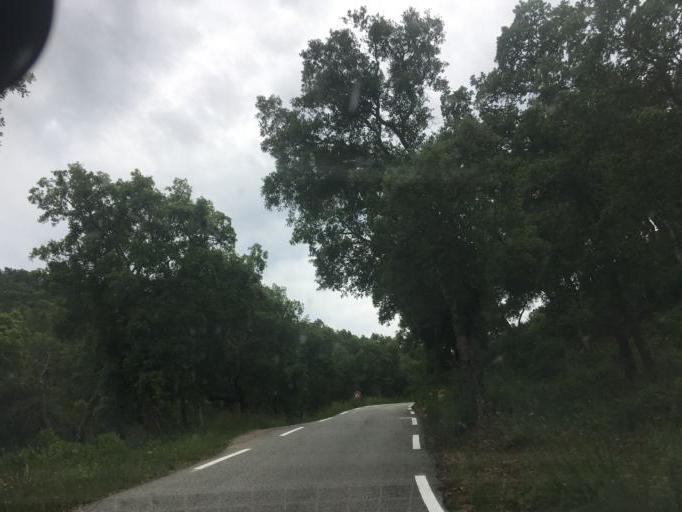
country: FR
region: Provence-Alpes-Cote d'Azur
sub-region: Departement du Var
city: Pignans
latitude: 43.2256
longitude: 6.2217
